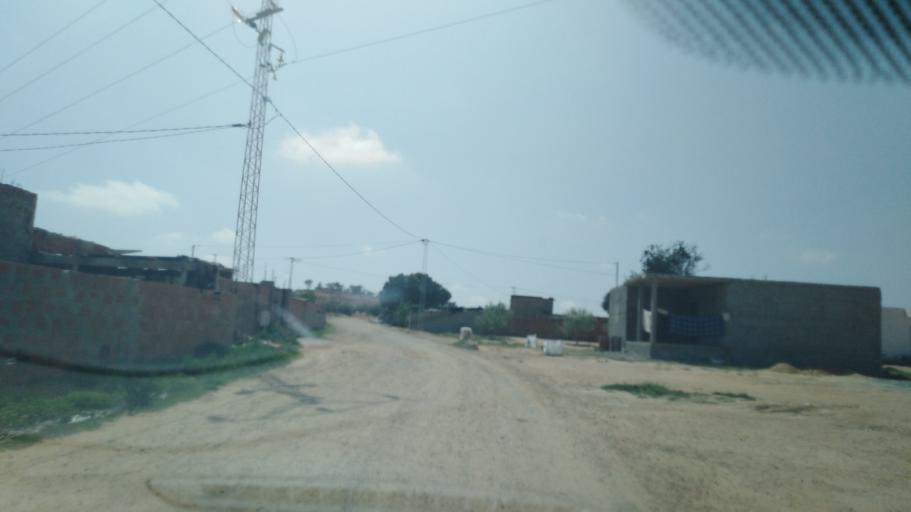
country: TN
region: Safaqis
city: Sfax
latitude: 34.7291
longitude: 10.5680
